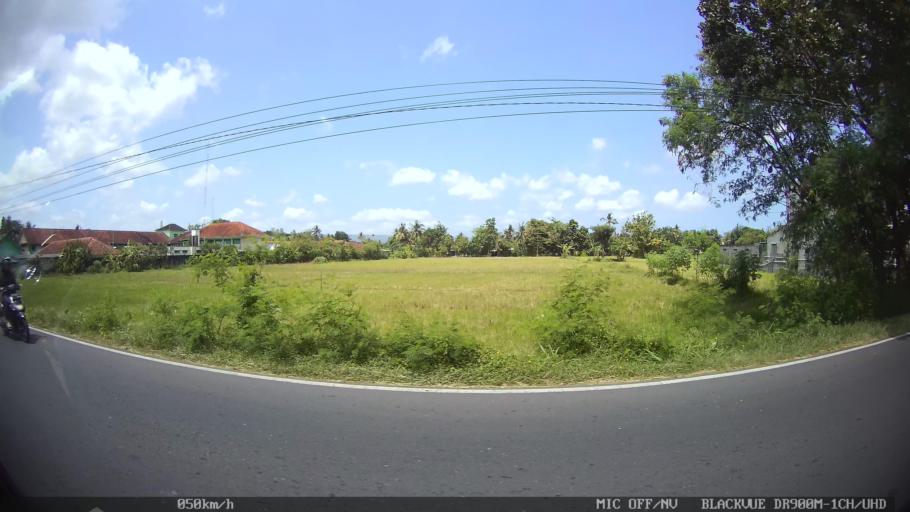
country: ID
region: Daerah Istimewa Yogyakarta
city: Bantul
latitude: -7.9048
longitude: 110.3304
